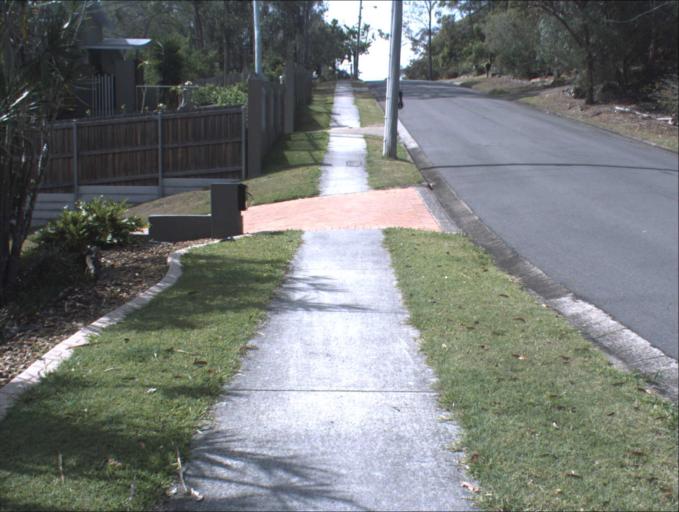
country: AU
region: Queensland
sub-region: Logan
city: Slacks Creek
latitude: -27.6264
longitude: 153.1518
